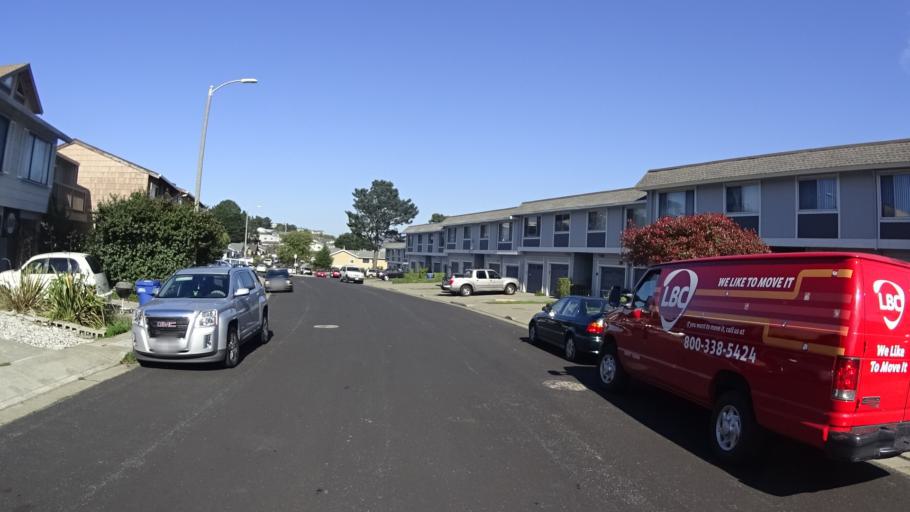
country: US
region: California
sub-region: San Mateo County
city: Colma
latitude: 37.6489
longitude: -122.4578
